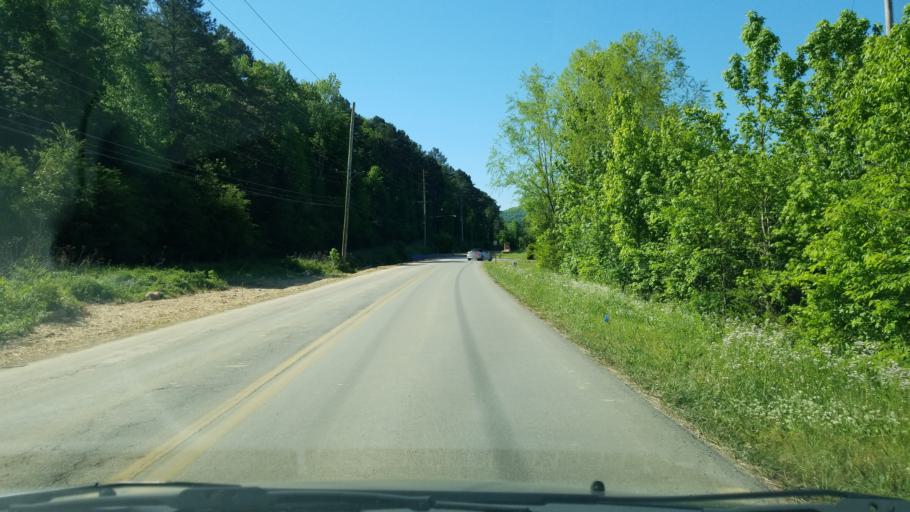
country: US
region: Tennessee
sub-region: Hamilton County
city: Chattanooga
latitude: 35.0457
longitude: -85.3334
